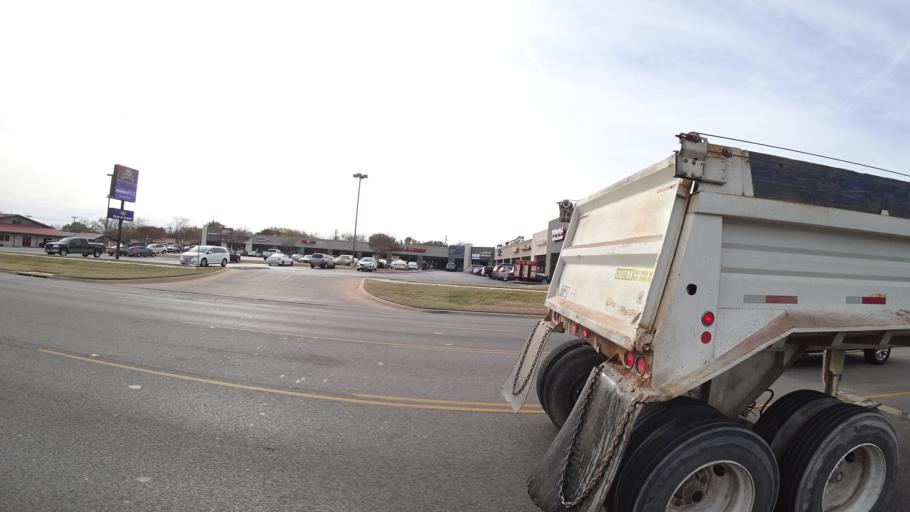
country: US
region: Texas
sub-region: Williamson County
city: Cedar Park
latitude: 30.5117
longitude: -97.8241
